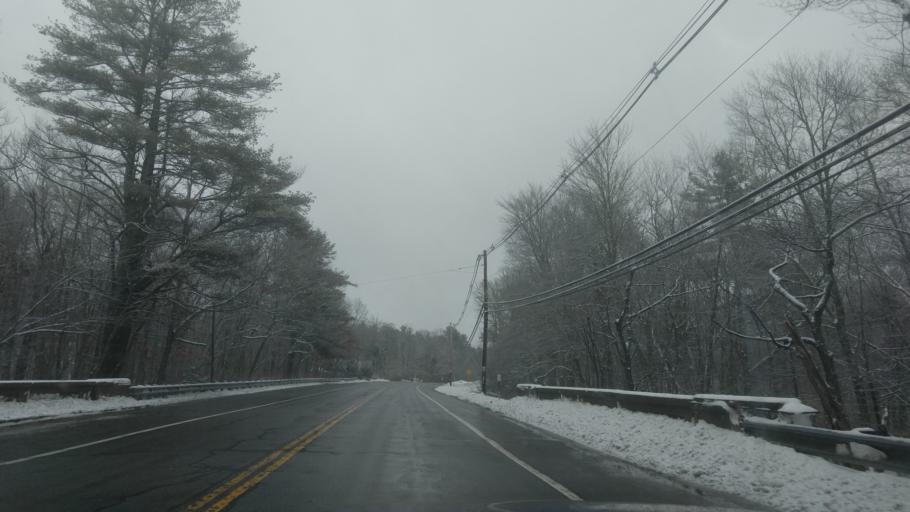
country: US
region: Rhode Island
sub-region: Providence County
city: Foster
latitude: 41.8210
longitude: -71.7056
